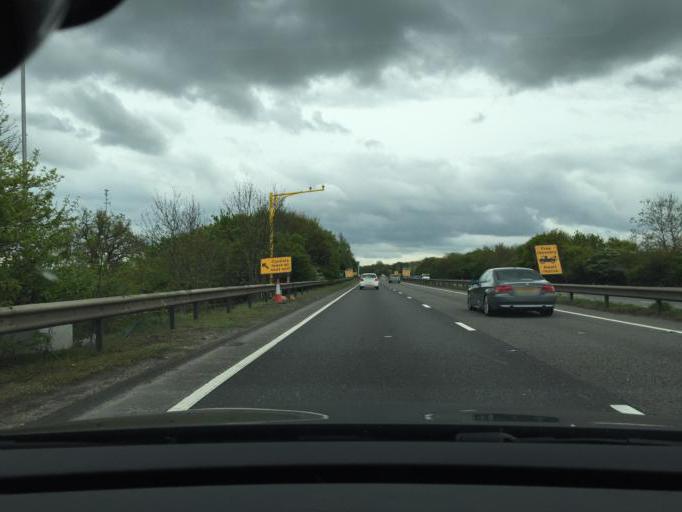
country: GB
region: England
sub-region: Oxfordshire
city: Harwell
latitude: 51.6243
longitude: -1.3073
